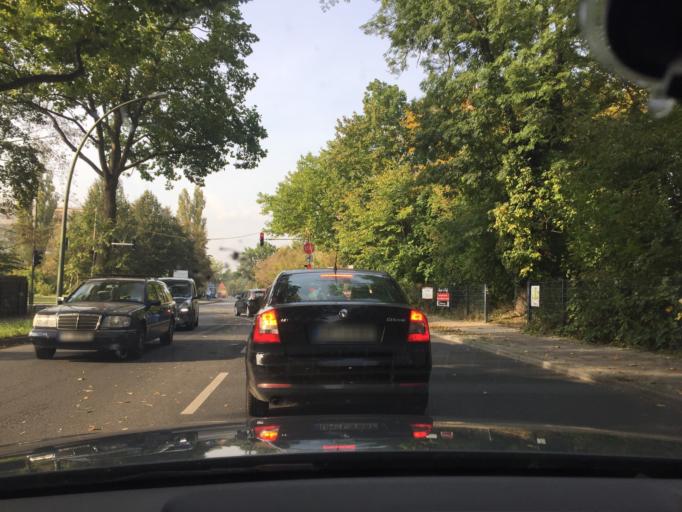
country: DE
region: Berlin
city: Buch
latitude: 52.6324
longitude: 13.5009
